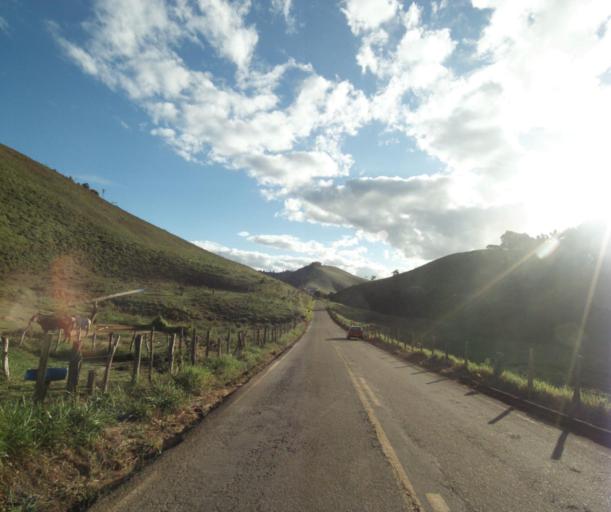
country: BR
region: Espirito Santo
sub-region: Guacui
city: Guacui
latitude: -20.6144
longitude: -41.6768
